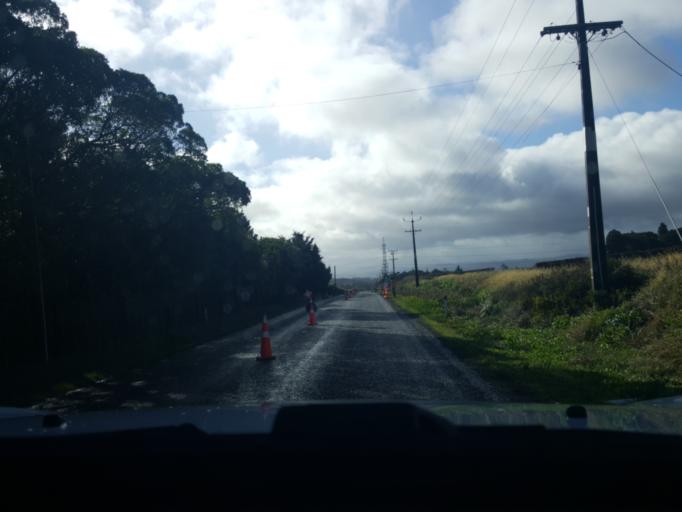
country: NZ
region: Auckland
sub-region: Auckland
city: Pukekohe East
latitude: -37.3093
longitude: 174.9903
